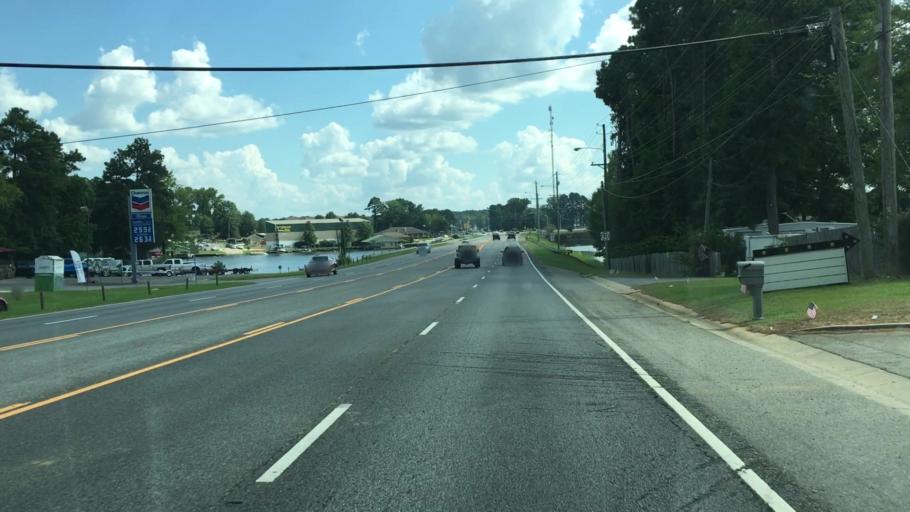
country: US
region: Georgia
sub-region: Baldwin County
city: Milledgeville
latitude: 33.1990
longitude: -83.2954
